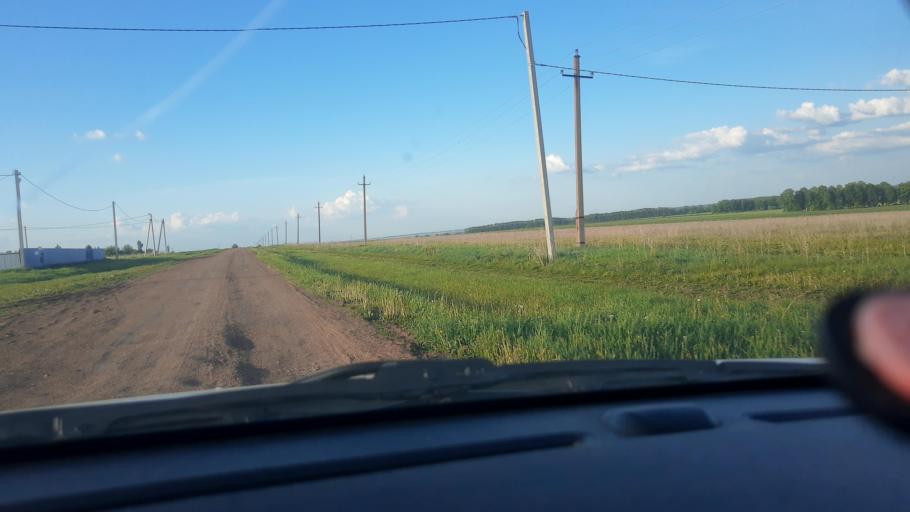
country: RU
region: Bashkortostan
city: Karmaskaly
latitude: 54.3848
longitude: 55.9414
